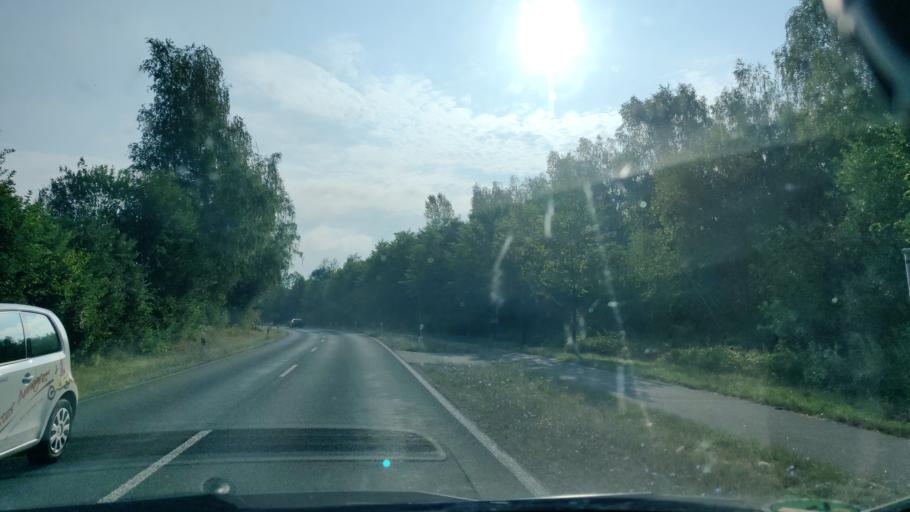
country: DE
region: Saxony
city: Borna
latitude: 51.0985
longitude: 12.5339
